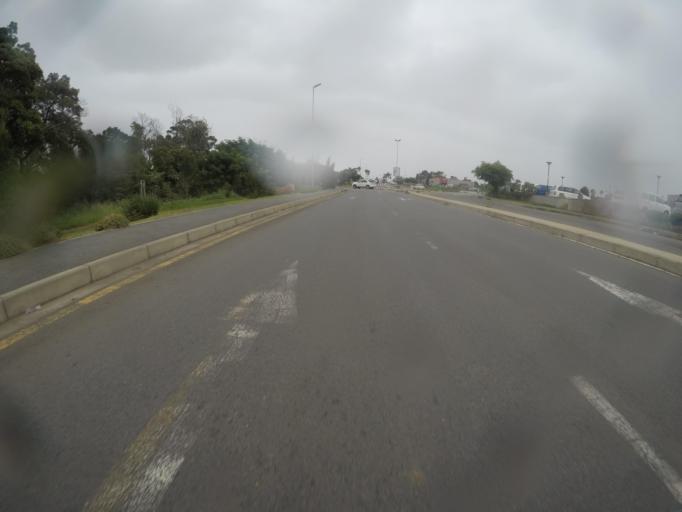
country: ZA
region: Eastern Cape
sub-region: Buffalo City Metropolitan Municipality
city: East London
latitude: -32.9369
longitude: 27.9933
